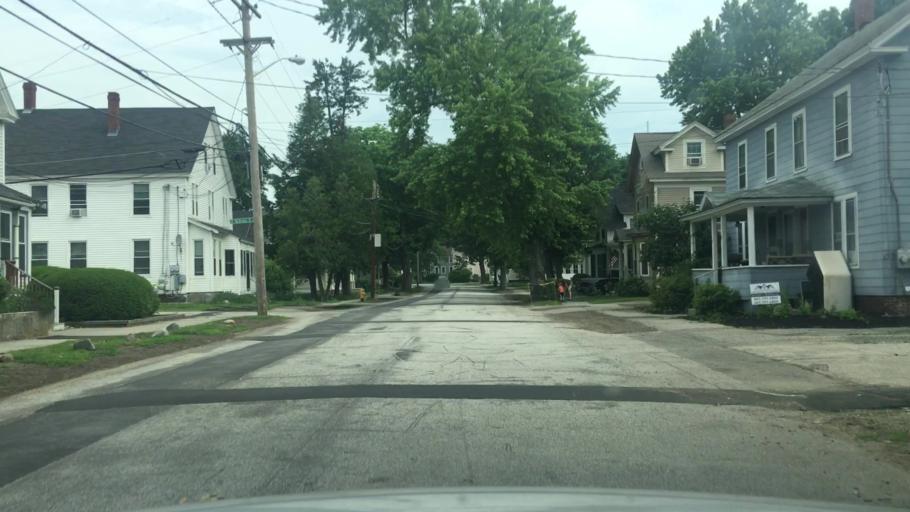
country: US
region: New Hampshire
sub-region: Rockingham County
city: Exeter
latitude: 42.9803
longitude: -70.9649
